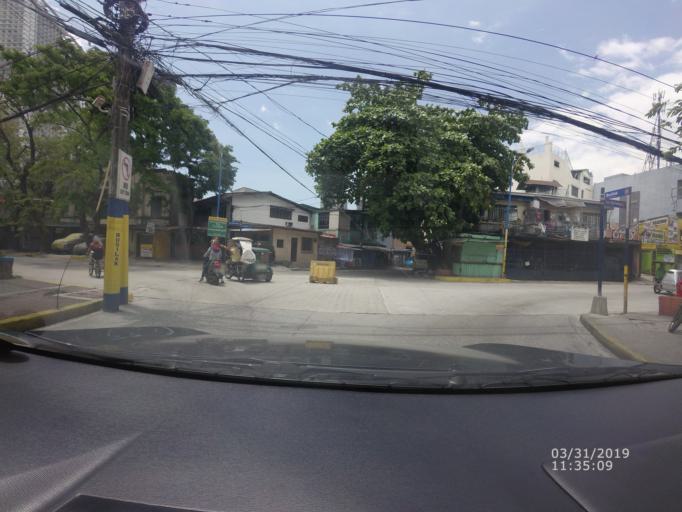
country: PH
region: Metro Manila
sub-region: Mandaluyong
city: Mandaluyong City
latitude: 14.5705
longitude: 121.0360
